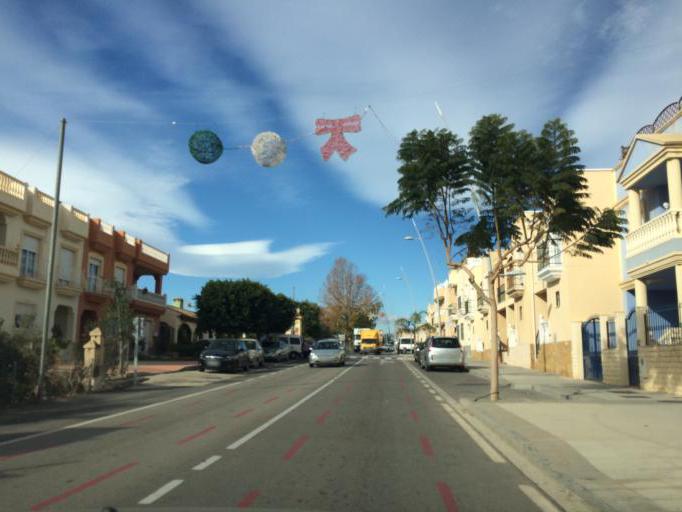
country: ES
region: Andalusia
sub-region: Provincia de Almeria
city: Rioja
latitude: 36.9456
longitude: -2.4644
